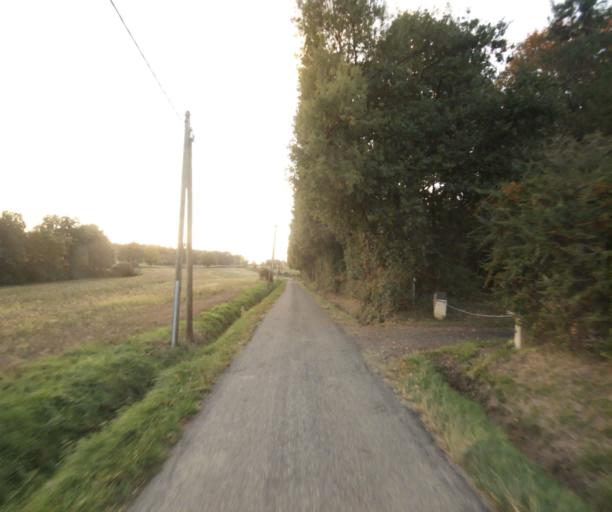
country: FR
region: Midi-Pyrenees
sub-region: Departement du Gers
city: Vic-Fezensac
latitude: 43.7848
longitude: 0.2461
